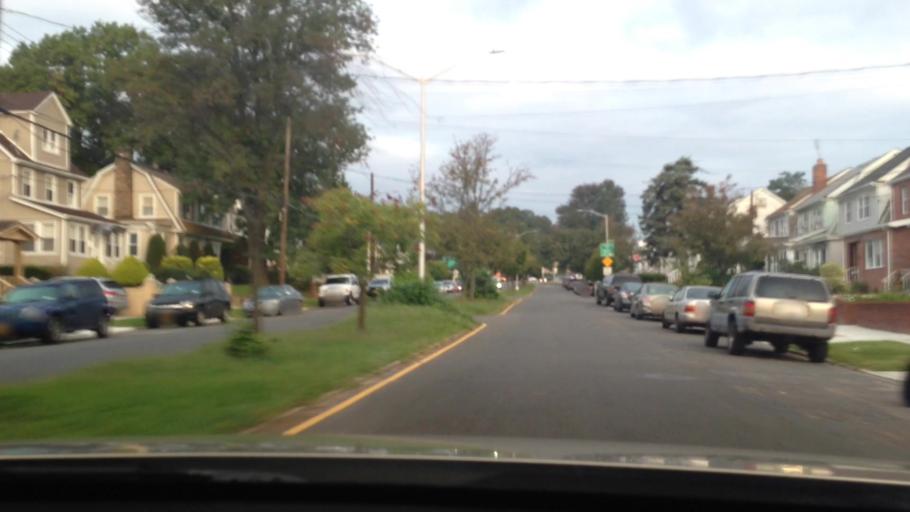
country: US
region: New York
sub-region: Nassau County
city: Bellerose Terrace
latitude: 40.7223
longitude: -73.7527
